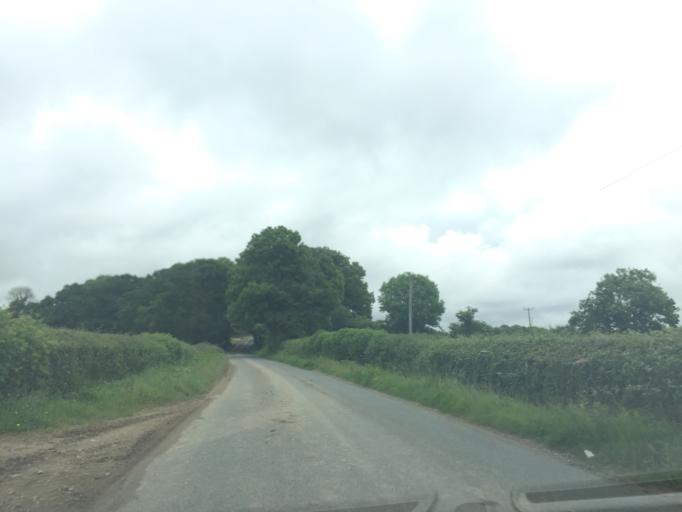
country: GB
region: England
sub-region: Dorset
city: Bovington Camp
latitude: 50.7193
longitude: -2.2951
